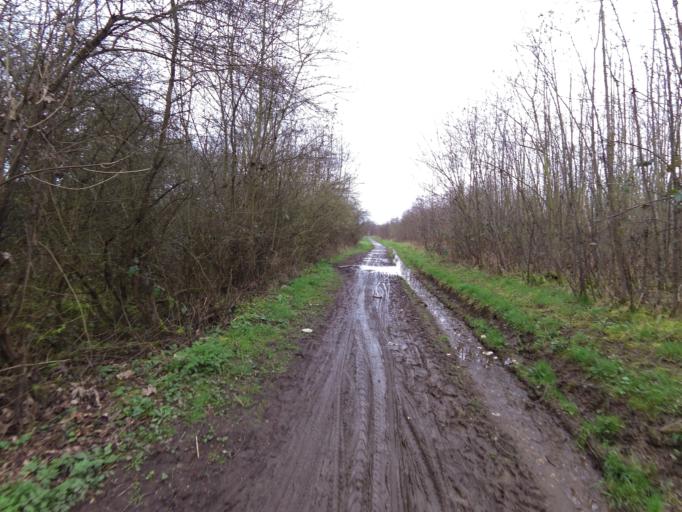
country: GB
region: England
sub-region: Doncaster
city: Bentley
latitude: 53.5606
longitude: -1.1513
